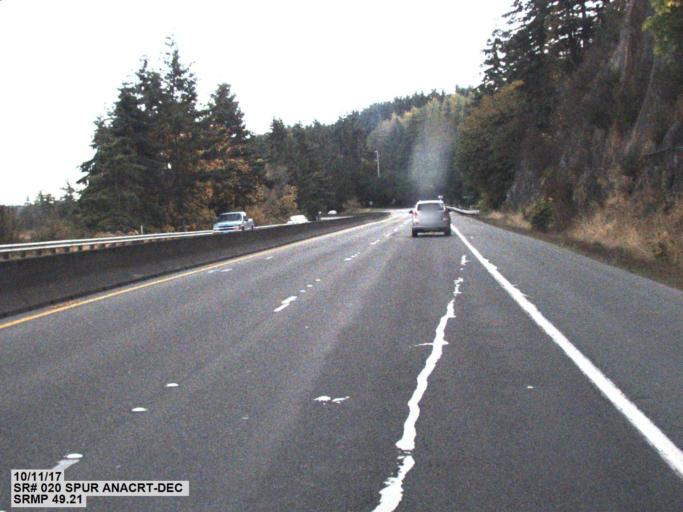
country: US
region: Washington
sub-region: Jefferson County
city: Port Hadlock-Irondale
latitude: 47.9901
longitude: -122.8618
